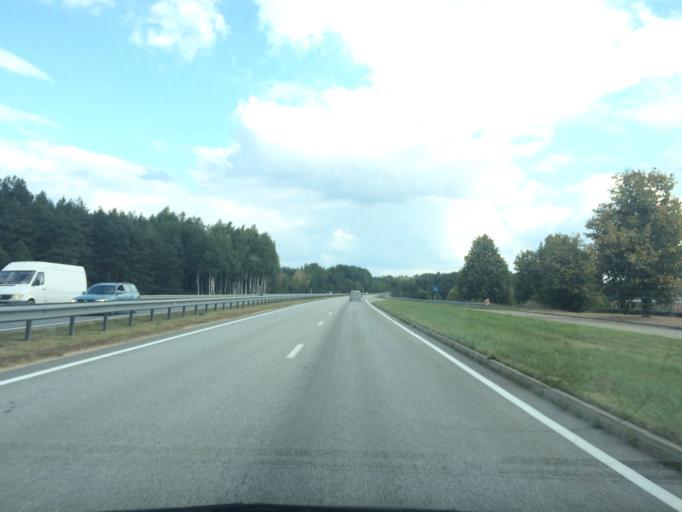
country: LV
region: Ikskile
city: Ikskile
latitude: 56.8450
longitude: 24.4720
